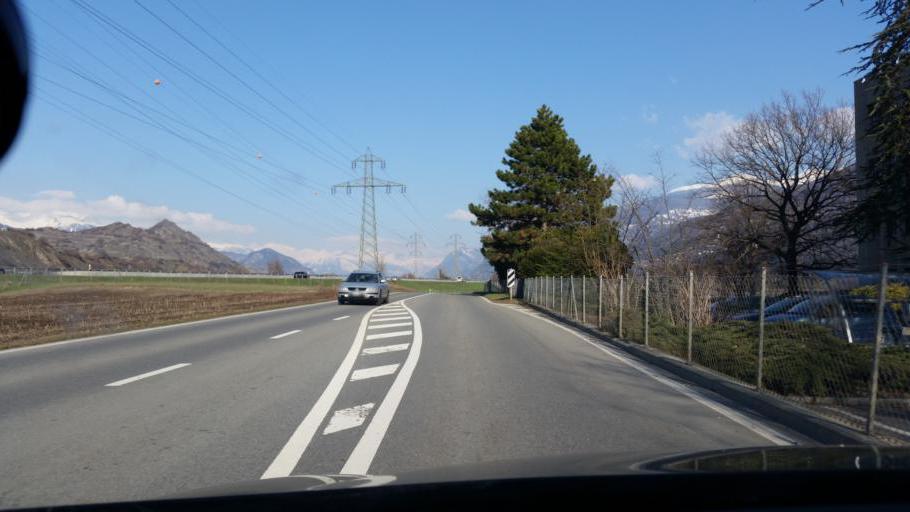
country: CH
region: Valais
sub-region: Conthey District
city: Conthey
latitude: 46.2123
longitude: 7.3027
